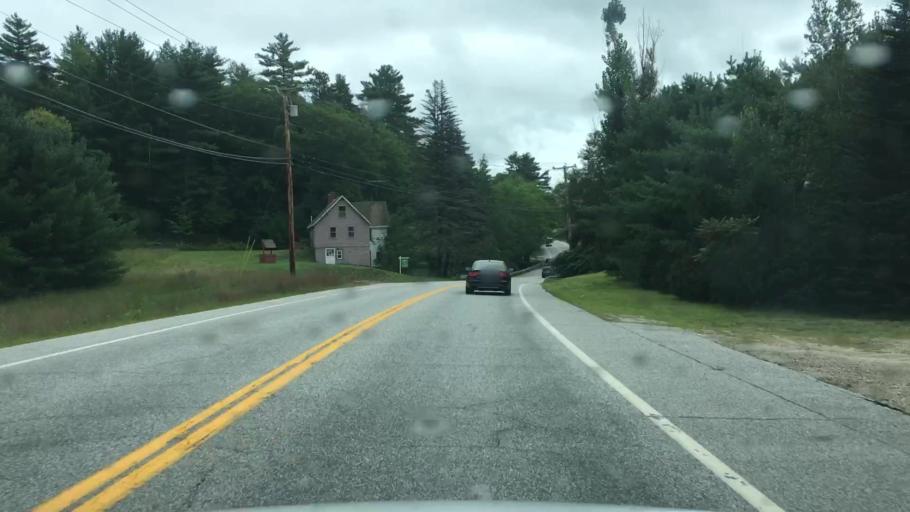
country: US
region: Maine
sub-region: York County
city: Cornish
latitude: 43.8273
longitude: -70.7759
